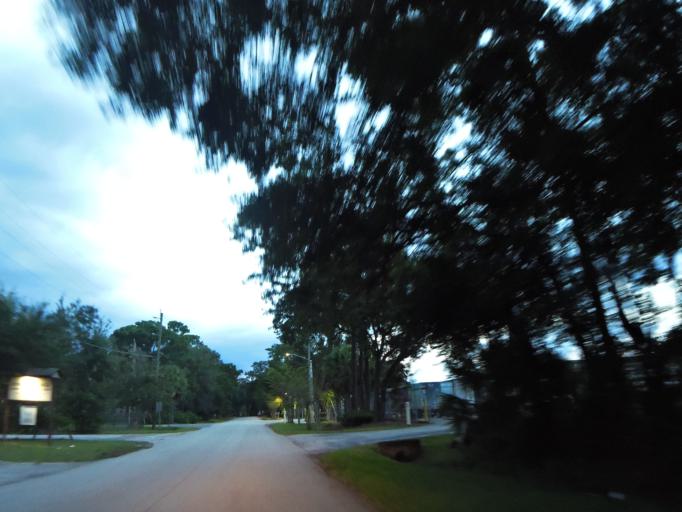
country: US
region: Florida
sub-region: Duval County
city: Jacksonville
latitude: 30.2591
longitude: -81.6085
